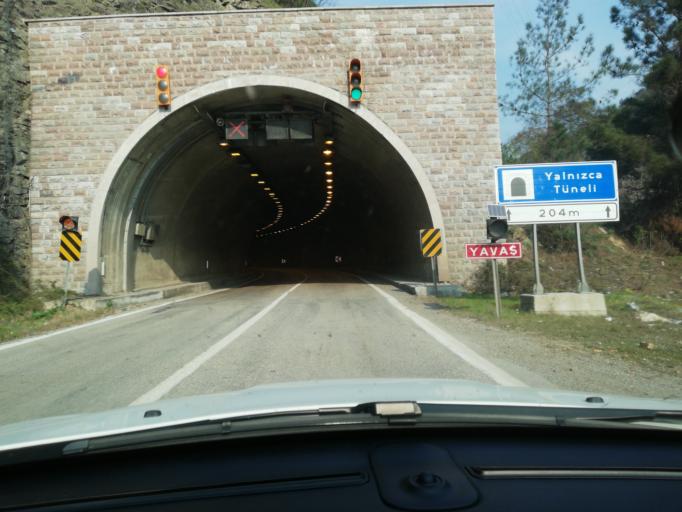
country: TR
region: Karabuk
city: Karabuk
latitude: 41.1530
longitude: 32.5274
